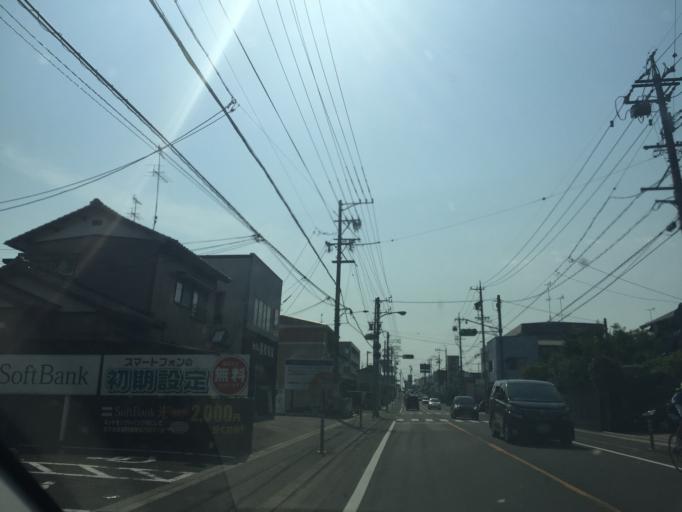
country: JP
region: Shizuoka
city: Kakegawa
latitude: 34.7712
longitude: 138.0027
